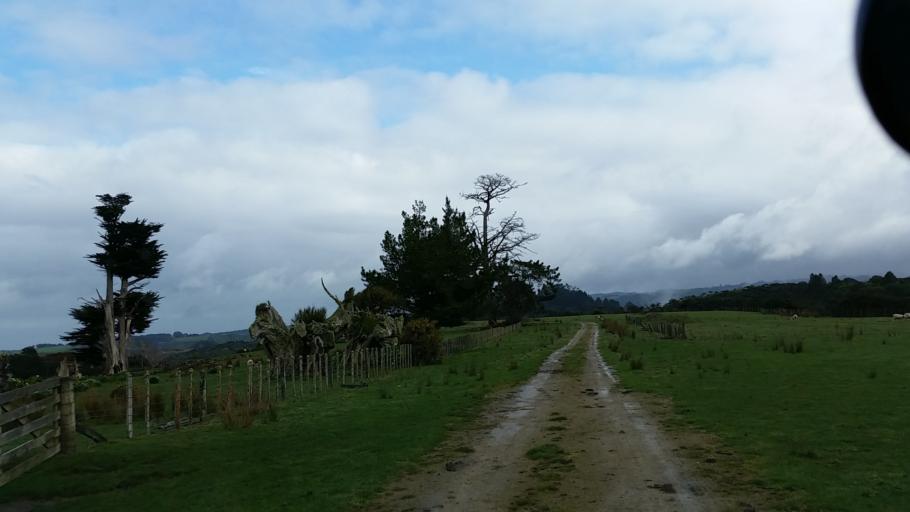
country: NZ
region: Taranaki
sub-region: South Taranaki District
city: Patea
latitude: -39.7179
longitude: 174.7634
